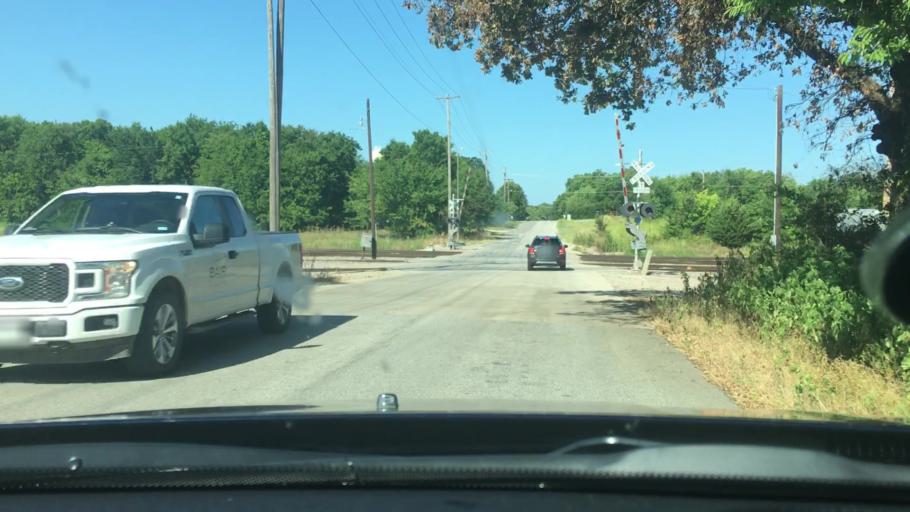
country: US
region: Oklahoma
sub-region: Marshall County
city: Madill
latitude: 34.0956
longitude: -96.7661
